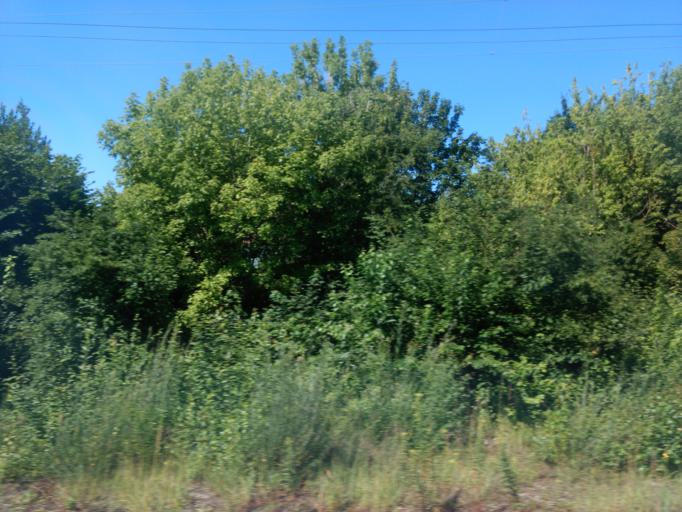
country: DE
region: Bavaria
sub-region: Upper Bavaria
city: Unterfoehring
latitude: 48.1675
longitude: 11.6461
